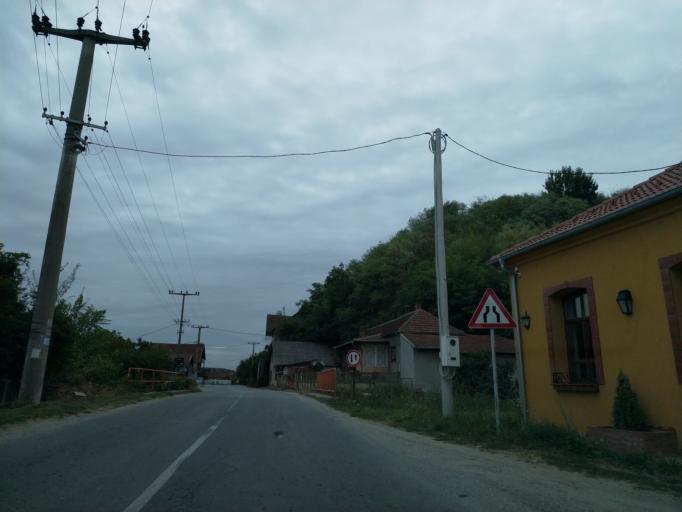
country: RS
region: Central Serbia
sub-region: Sumadijski Okrug
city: Batocina
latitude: 44.1061
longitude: 21.1592
